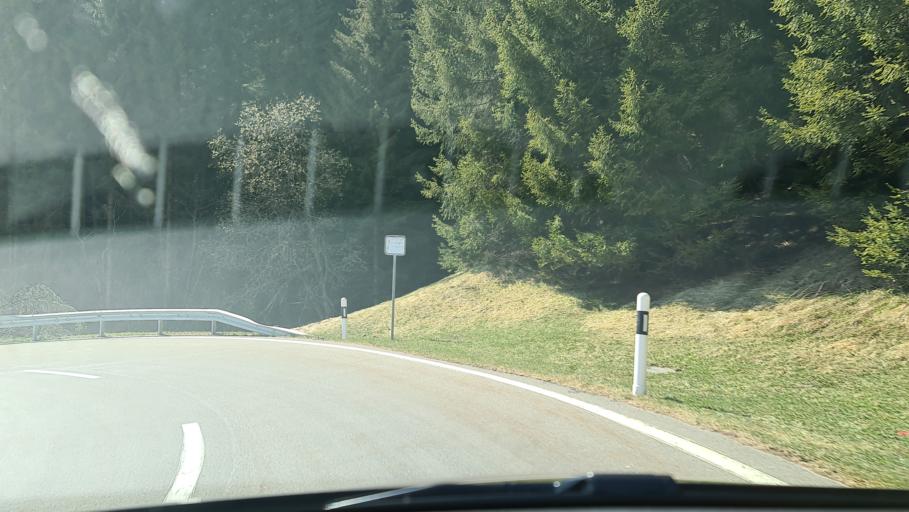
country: CH
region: Grisons
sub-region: Moesa District
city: Mesocco
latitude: 46.4349
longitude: 9.2149
